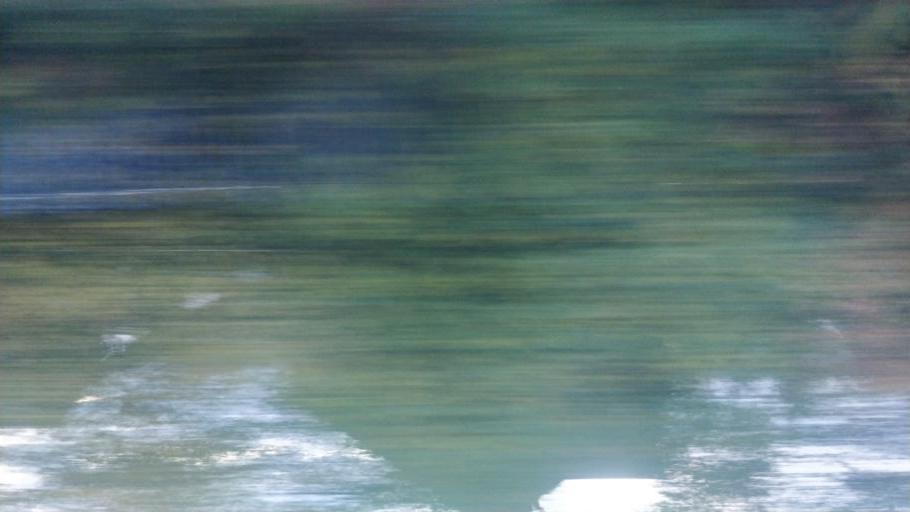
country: GB
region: England
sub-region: Lancashire
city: Appley Bridge
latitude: 53.5762
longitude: -2.7147
